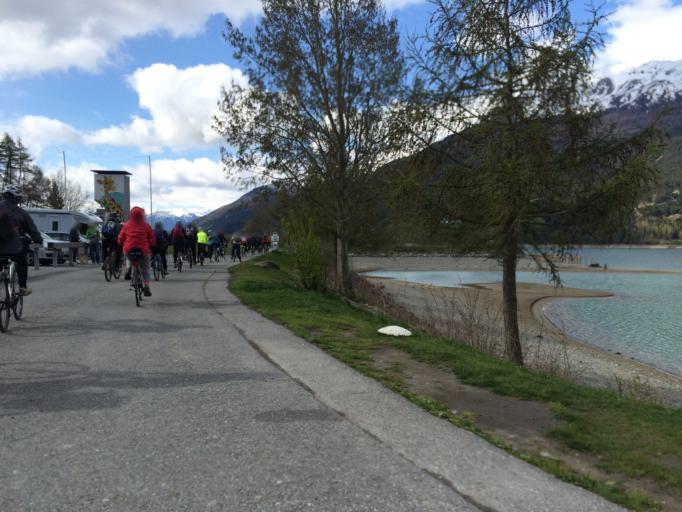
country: IT
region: Trentino-Alto Adige
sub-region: Bolzano
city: Curon Venosta
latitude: 46.8107
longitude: 10.5378
